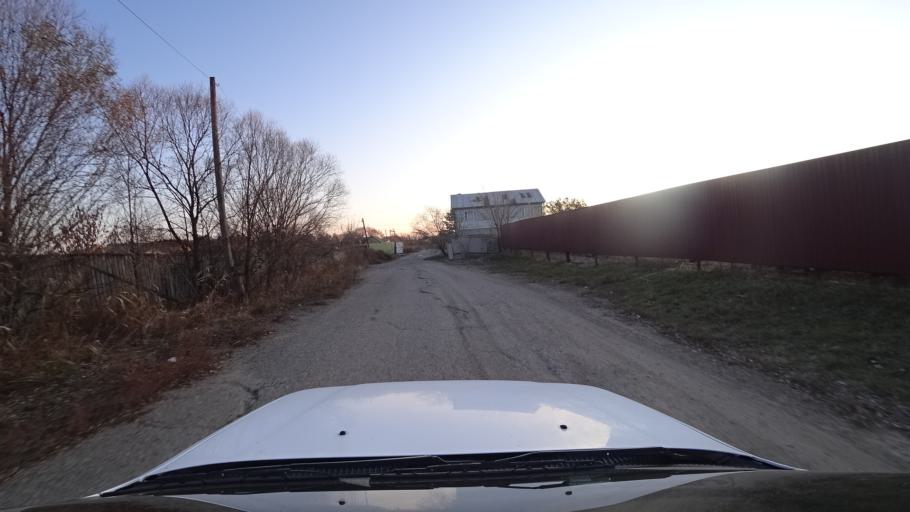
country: RU
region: Primorskiy
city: Dal'nerechensk
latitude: 45.9184
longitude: 133.7359
